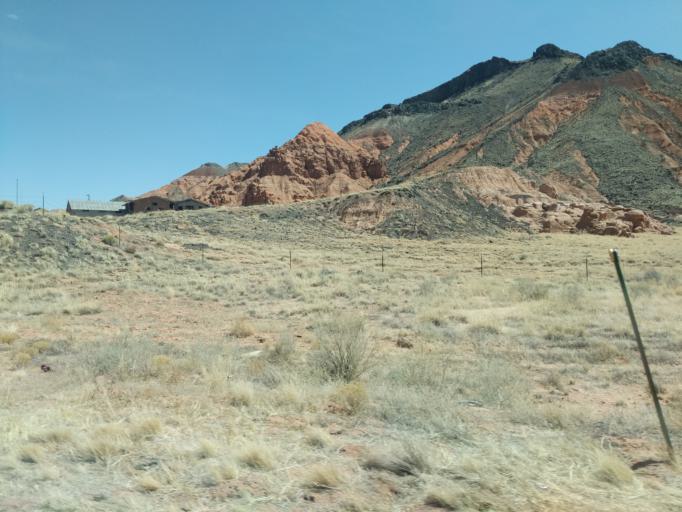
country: US
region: Arizona
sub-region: Navajo County
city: Dilkon
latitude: 35.4047
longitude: -110.0649
